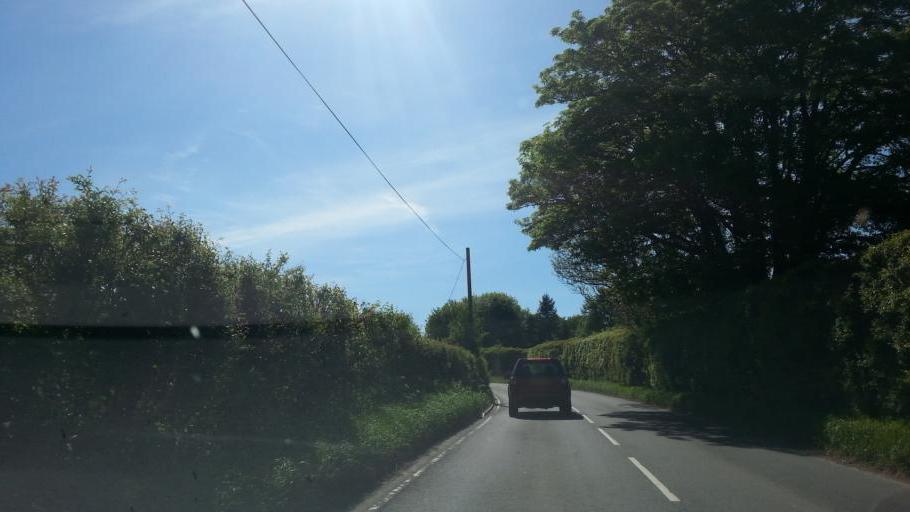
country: GB
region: England
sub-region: Dorset
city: Gillingham
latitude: 51.0032
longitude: -2.3044
